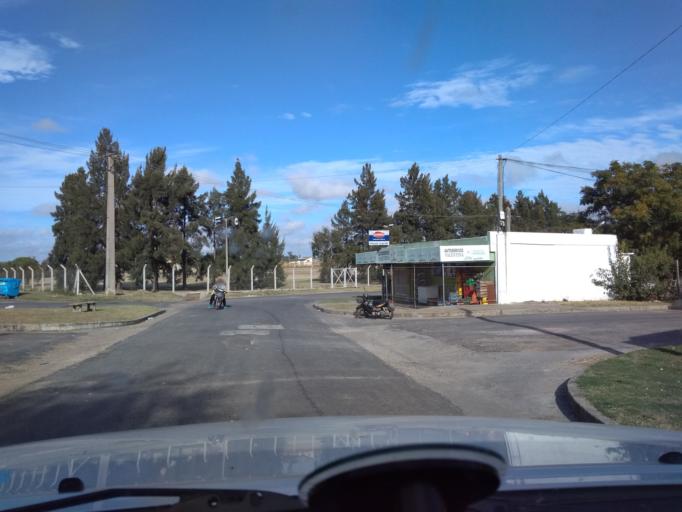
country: UY
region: Florida
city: Florida
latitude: -34.1072
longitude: -56.2152
